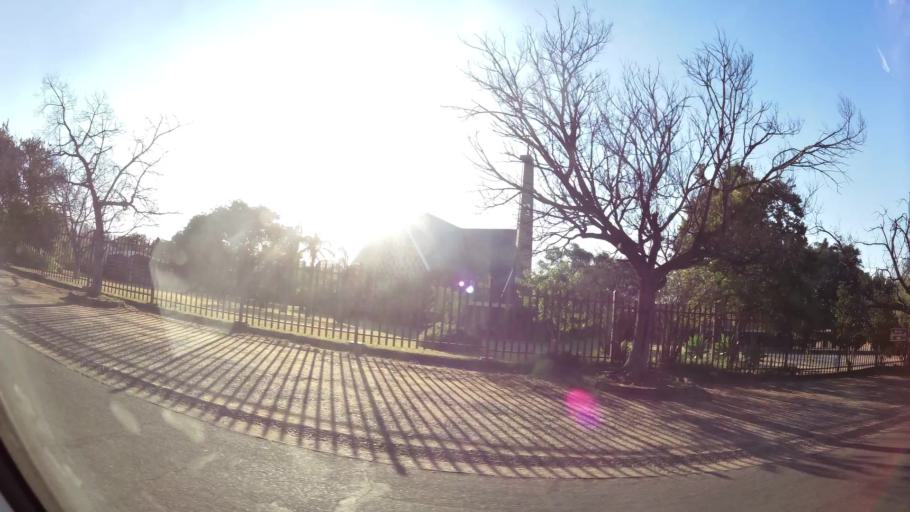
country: ZA
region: North-West
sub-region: Bojanala Platinum District Municipality
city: Rustenburg
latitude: -25.6803
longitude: 27.2273
